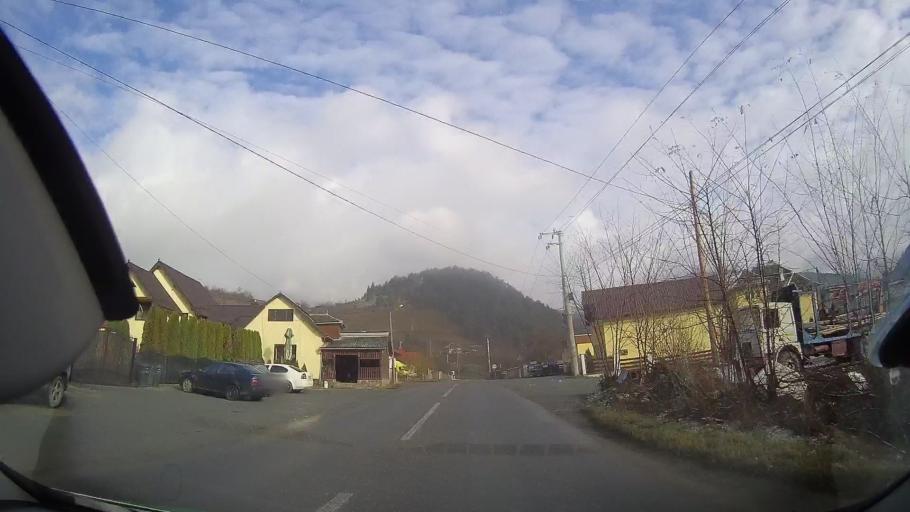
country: RO
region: Alba
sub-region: Comuna Bistra
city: Bistra
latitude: 46.3781
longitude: 23.1182
